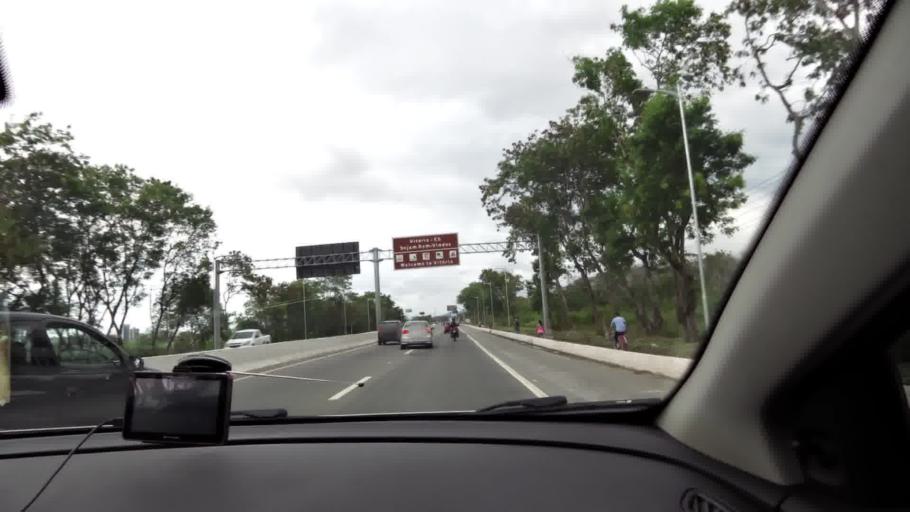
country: BR
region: Espirito Santo
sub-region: Vila Velha
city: Vila Velha
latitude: -20.2517
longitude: -40.2872
